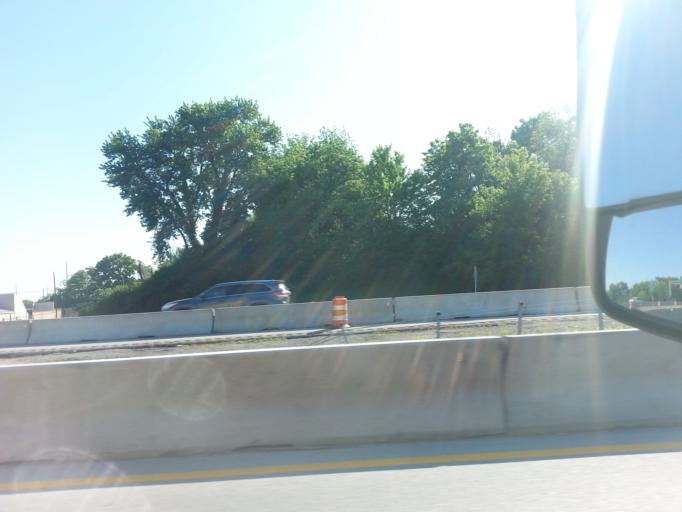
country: US
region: Indiana
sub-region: Clark County
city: Jeffersonville
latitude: 38.2556
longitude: -85.7209
